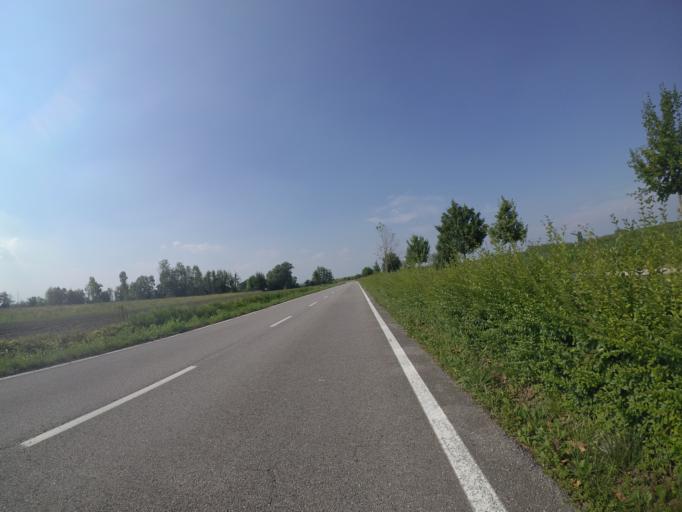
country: IT
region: Friuli Venezia Giulia
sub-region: Provincia di Udine
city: Camino al Tagliamento
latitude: 45.9218
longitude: 12.9640
